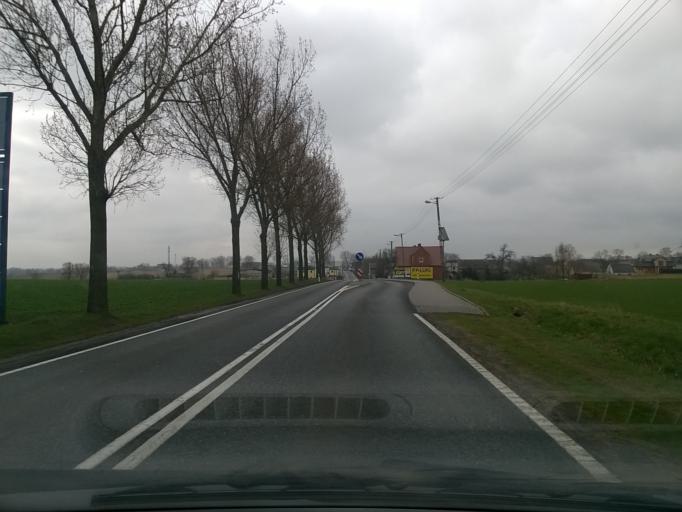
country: PL
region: Kujawsko-Pomorskie
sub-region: Powiat zninski
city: Znin
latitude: 52.8753
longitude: 17.6991
